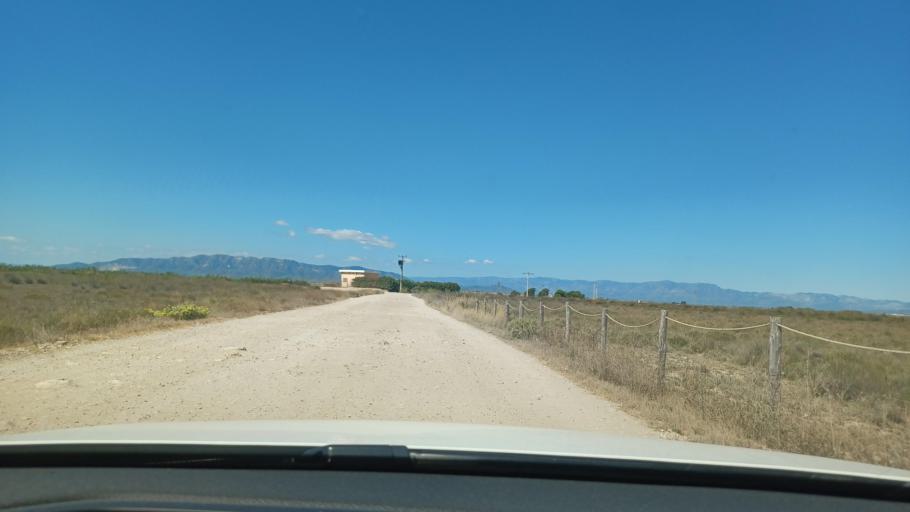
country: ES
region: Catalonia
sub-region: Provincia de Tarragona
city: Deltebre
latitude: 40.6483
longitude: 0.7663
